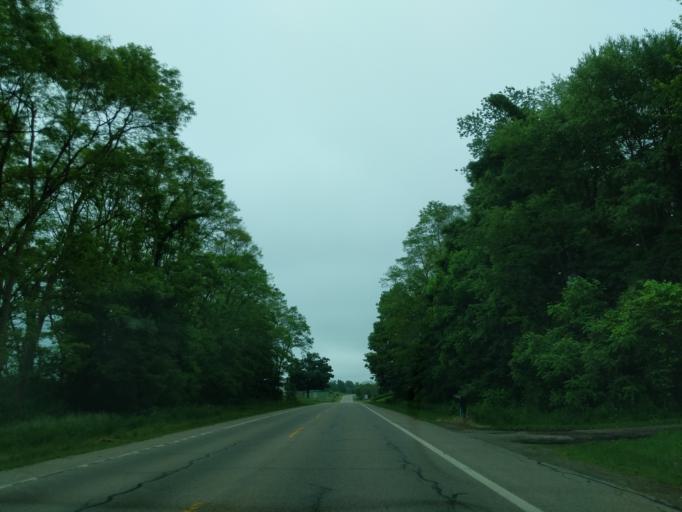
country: US
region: Michigan
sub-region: Hillsdale County
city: Litchfield
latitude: 42.0290
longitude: -84.7206
